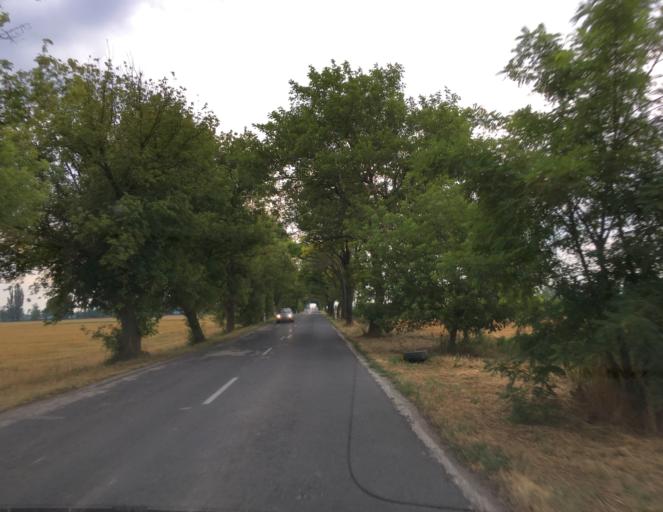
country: SK
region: Trnavsky
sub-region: Okres Dunajska Streda
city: Velky Meder
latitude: 47.9060
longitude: 17.7795
